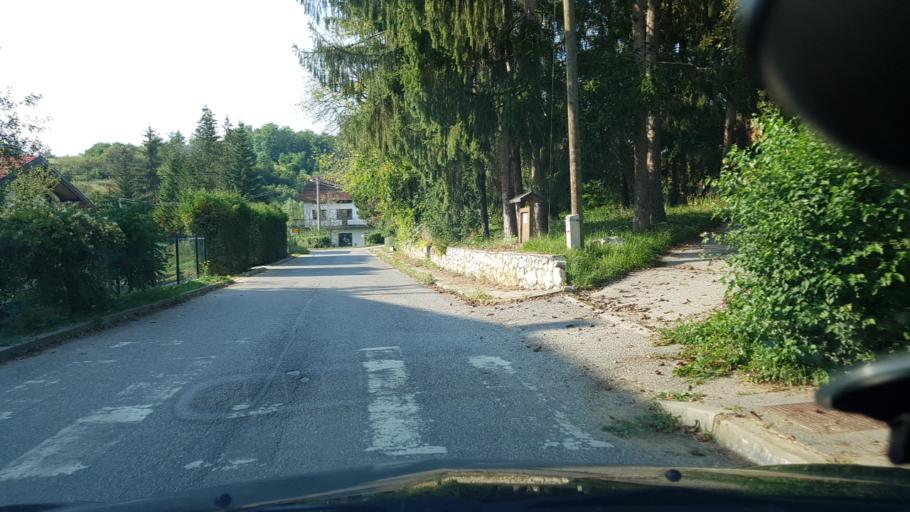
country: HR
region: Krapinsko-Zagorska
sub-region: Grad Krapina
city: Krapina
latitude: 46.1257
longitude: 15.8504
